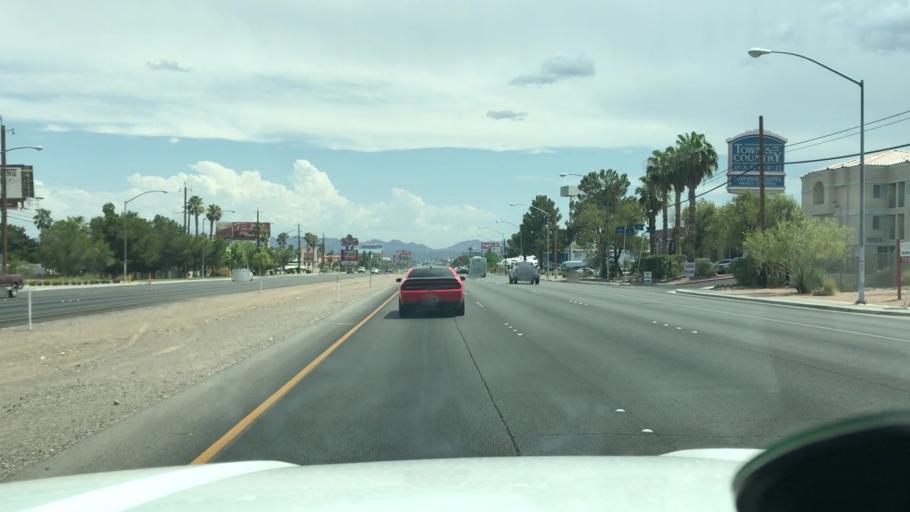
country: US
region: Nevada
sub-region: Clark County
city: Winchester
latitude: 36.1262
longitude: -115.0796
